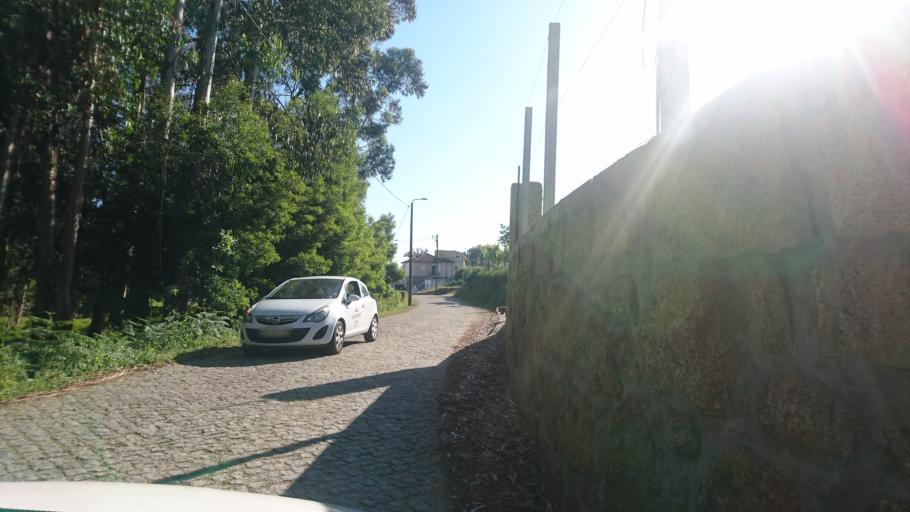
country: PT
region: Porto
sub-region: Paredes
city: Baltar
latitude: 41.1629
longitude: -8.3769
